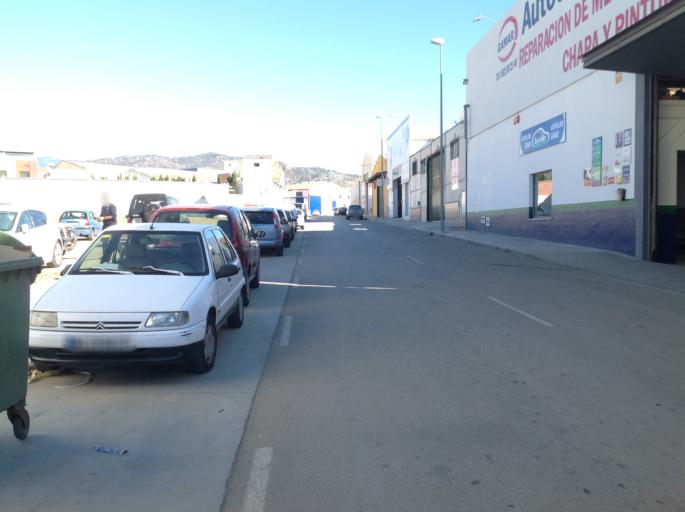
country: ES
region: Andalusia
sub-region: Provincia de Malaga
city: Velez-Malaga
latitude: 36.7649
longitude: -4.0940
